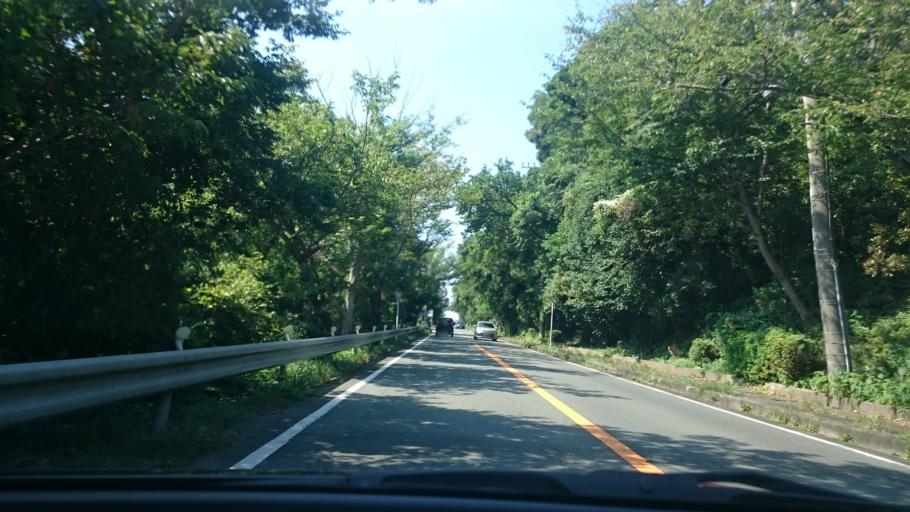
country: JP
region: Shizuoka
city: Heda
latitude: 34.8653
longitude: 138.7628
